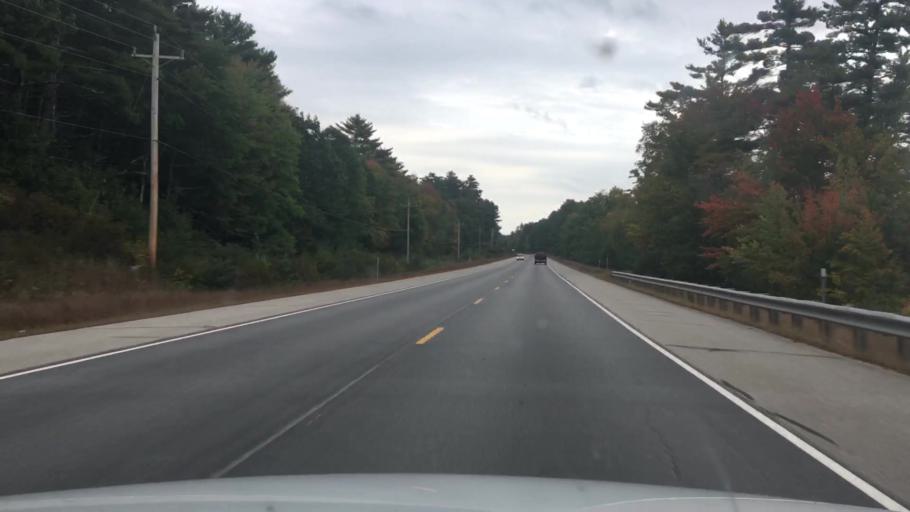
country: US
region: New Hampshire
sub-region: Strafford County
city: New Durham
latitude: 43.4457
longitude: -71.2011
